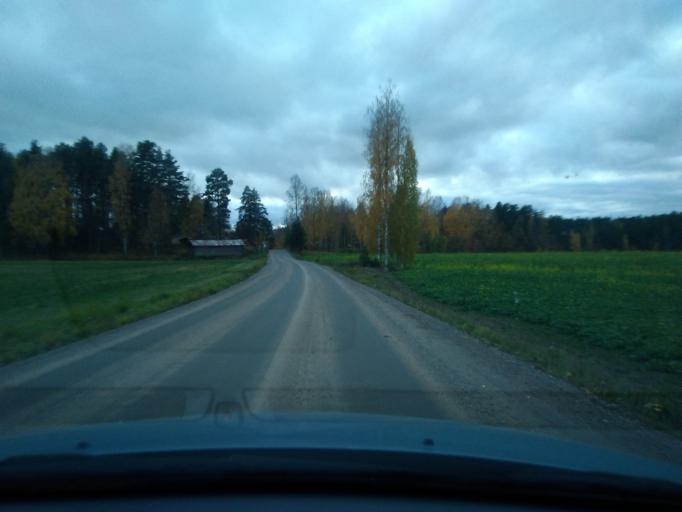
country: FI
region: Central Finland
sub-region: Saarijaervi-Viitasaari
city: Saarijaervi
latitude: 62.6923
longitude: 25.3195
